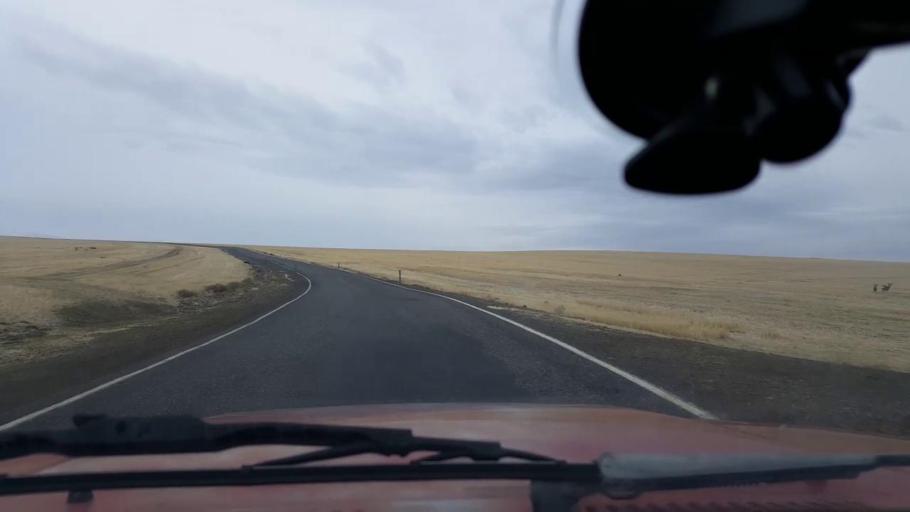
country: US
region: Washington
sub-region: Asotin County
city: Clarkston Heights-Vineland
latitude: 46.3453
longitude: -117.2543
